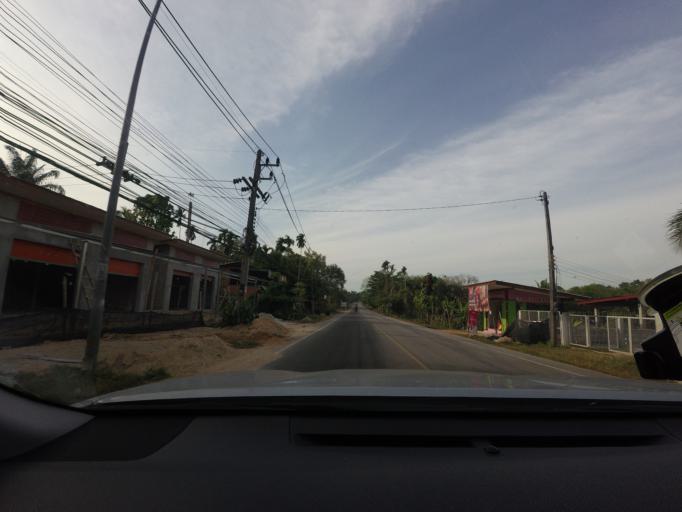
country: TH
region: Narathiwat
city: Ra-ngae
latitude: 6.2983
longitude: 101.7286
